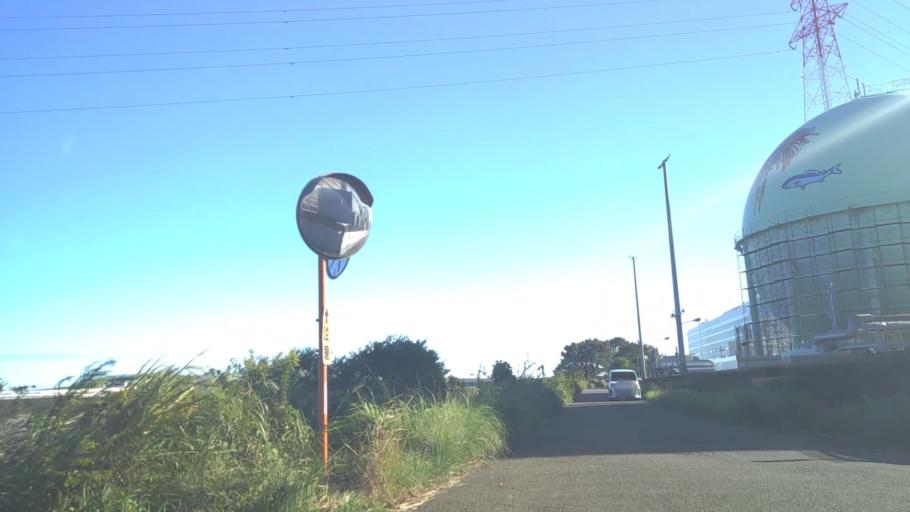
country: JP
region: Kanagawa
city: Atsugi
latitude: 35.4312
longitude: 139.3712
